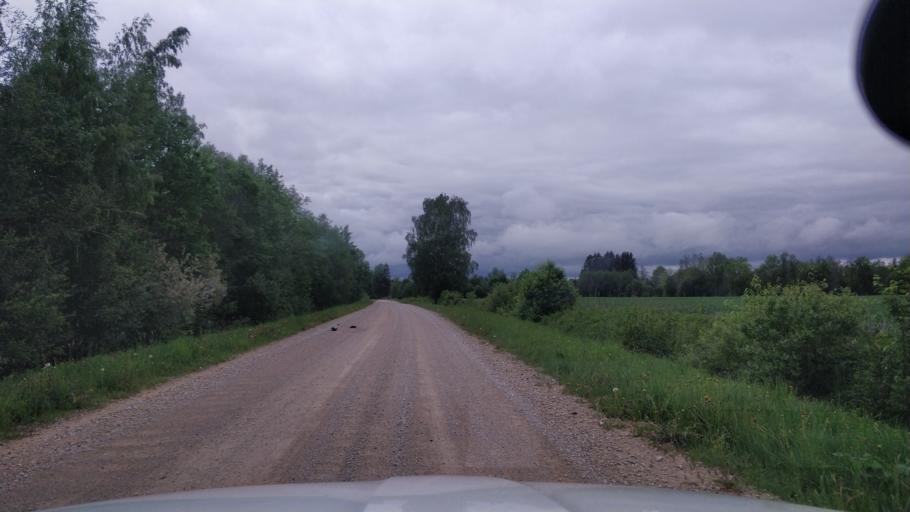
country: EE
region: Paernumaa
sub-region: Halinga vald
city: Parnu-Jaagupi
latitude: 58.7089
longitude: 24.3552
